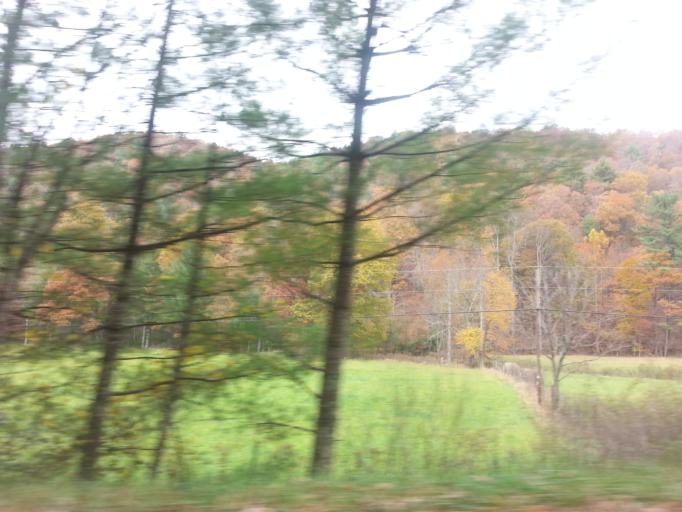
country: US
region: Virginia
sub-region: Bland County
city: Bland
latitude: 37.0766
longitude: -80.9550
